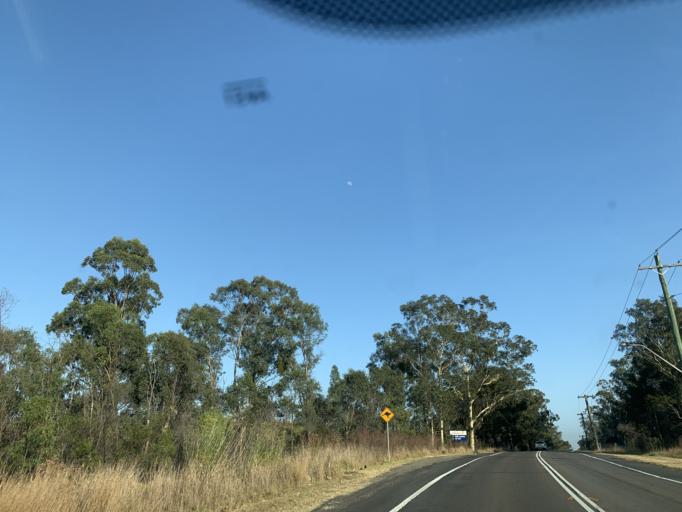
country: AU
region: New South Wales
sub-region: Fairfield
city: Horsley Park
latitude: -33.8302
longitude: 150.8731
